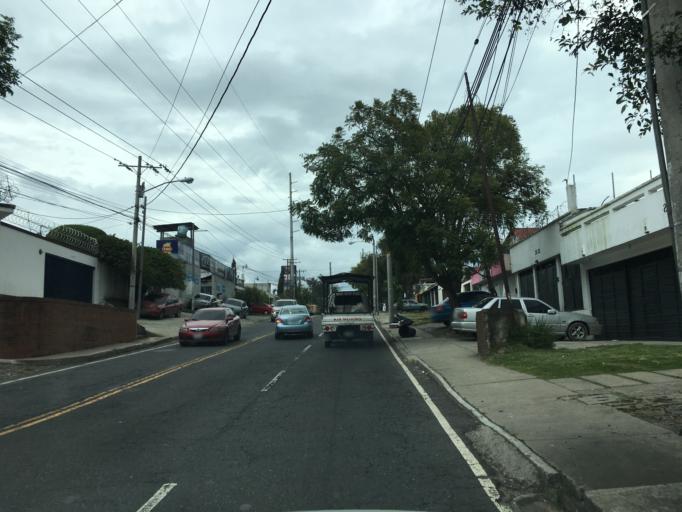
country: GT
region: Guatemala
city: Mixco
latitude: 14.6014
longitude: -90.5591
